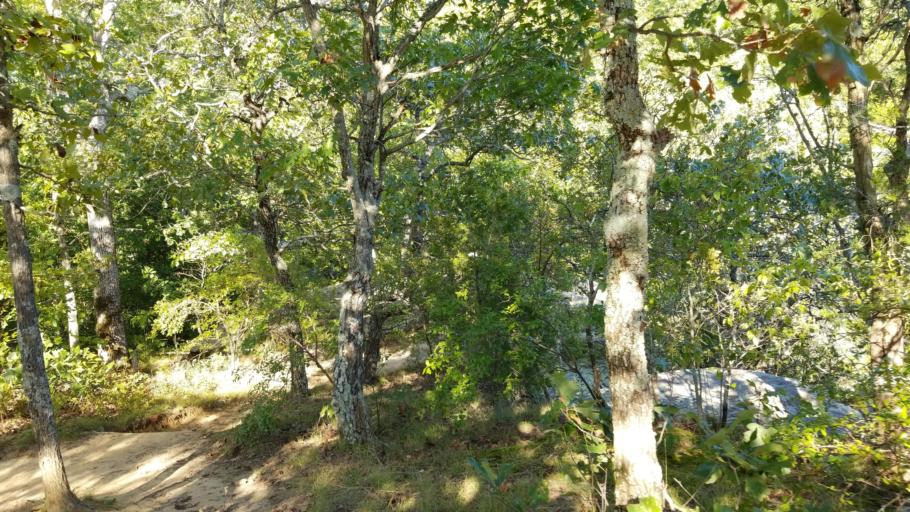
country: US
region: Illinois
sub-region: Hardin County
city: Elizabethtown
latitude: 37.6039
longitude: -88.3863
